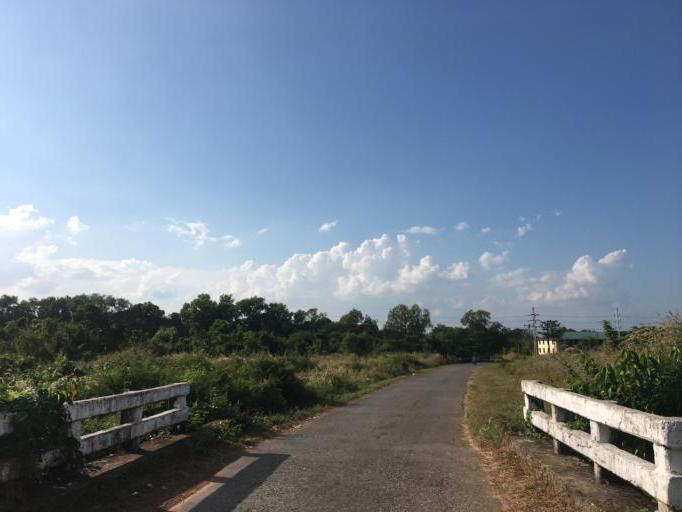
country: MM
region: Mon
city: Mawlamyine
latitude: 16.4363
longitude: 97.6559
